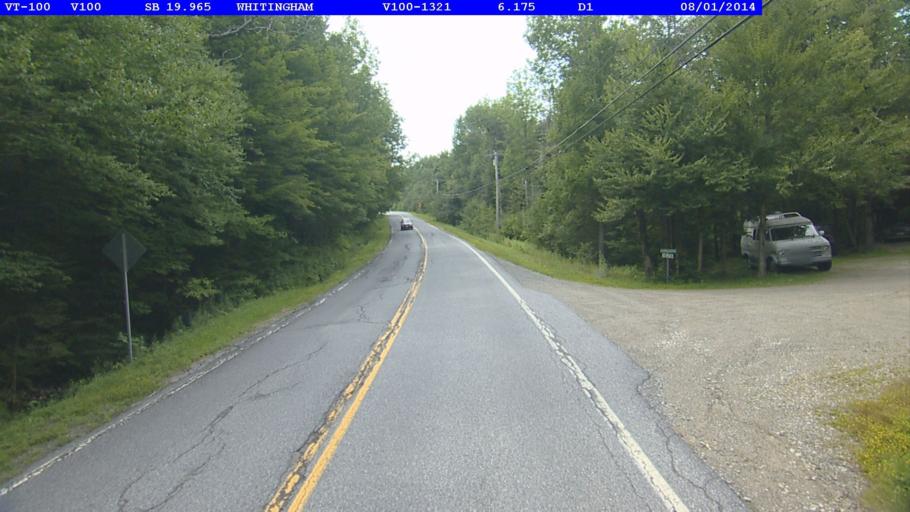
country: US
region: Vermont
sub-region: Windham County
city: Dover
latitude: 42.7879
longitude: -72.8457
